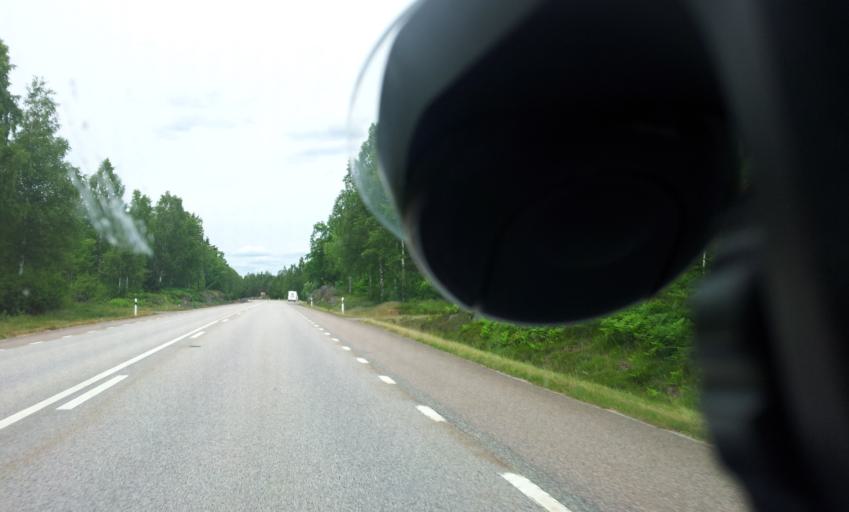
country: SE
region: Kalmar
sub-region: Oskarshamns Kommun
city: Oskarshamn
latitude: 57.5069
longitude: 16.5025
